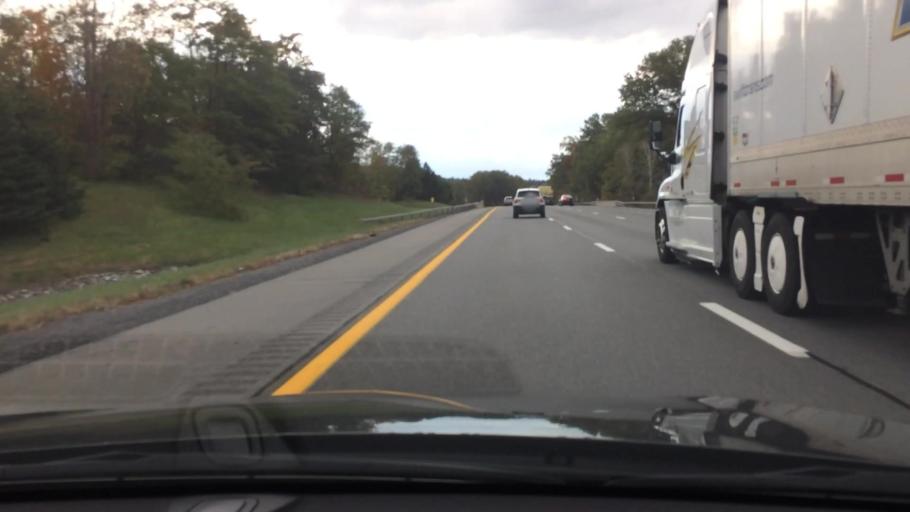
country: US
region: New York
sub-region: Saratoga County
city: Country Knolls
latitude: 42.9007
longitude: -73.7850
